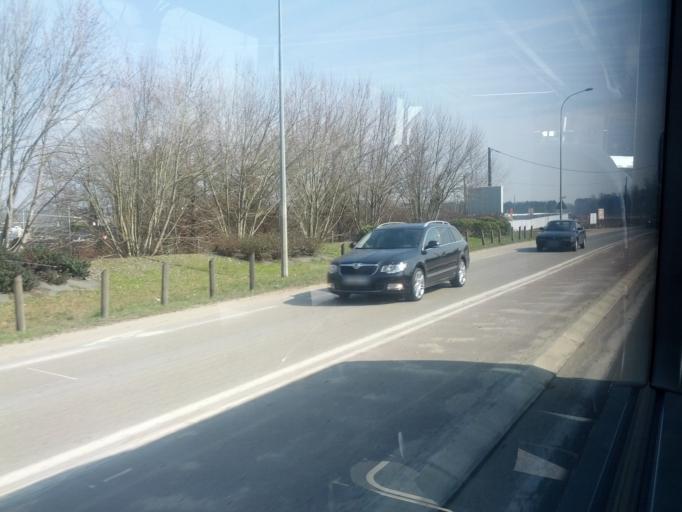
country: FR
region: Aquitaine
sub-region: Departement de la Gironde
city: Le Haillan
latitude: 44.8481
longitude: -0.7067
